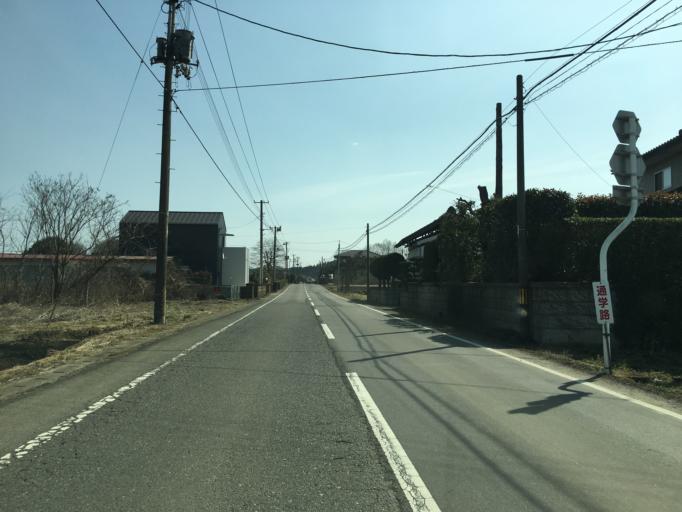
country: JP
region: Fukushima
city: Ishikawa
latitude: 37.1490
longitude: 140.3943
